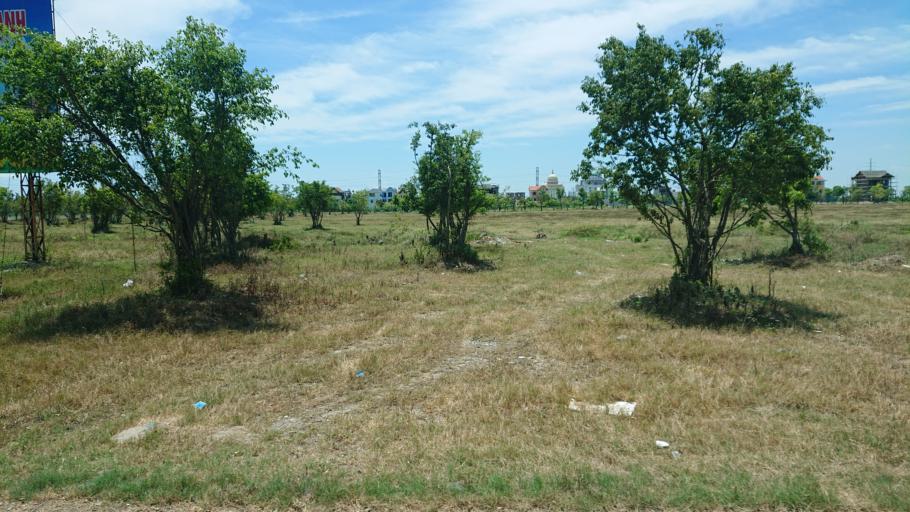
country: VN
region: Ninh Binh
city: Thanh Pho Ninh Binh
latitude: 20.2719
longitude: 105.9766
